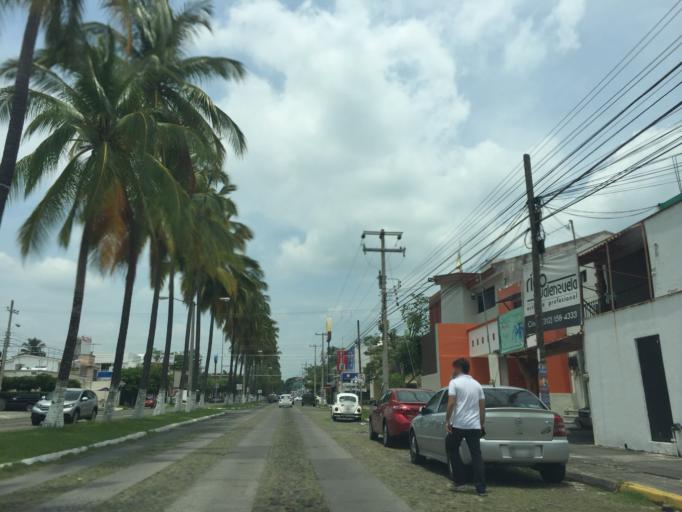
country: MX
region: Colima
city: Colima
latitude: 19.2549
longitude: -103.7179
